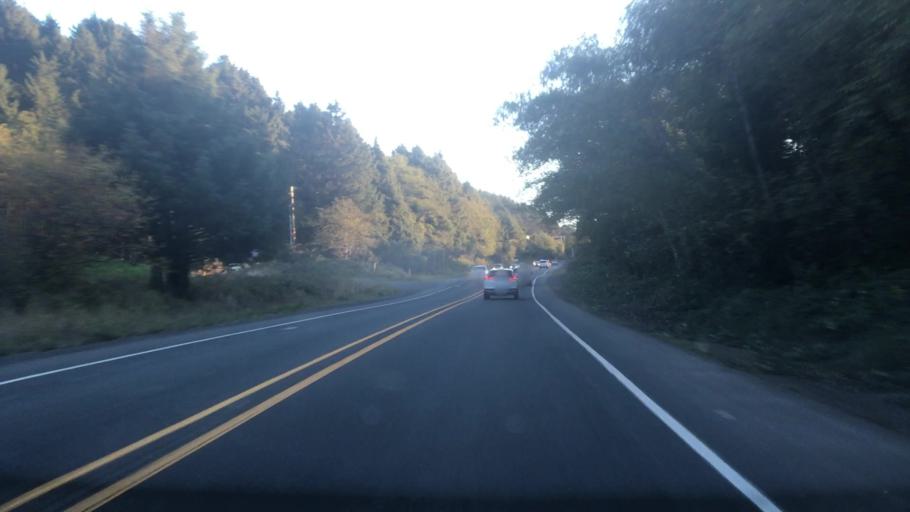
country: US
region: Oregon
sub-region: Clatsop County
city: Cannon Beach
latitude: 45.8638
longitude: -123.9592
